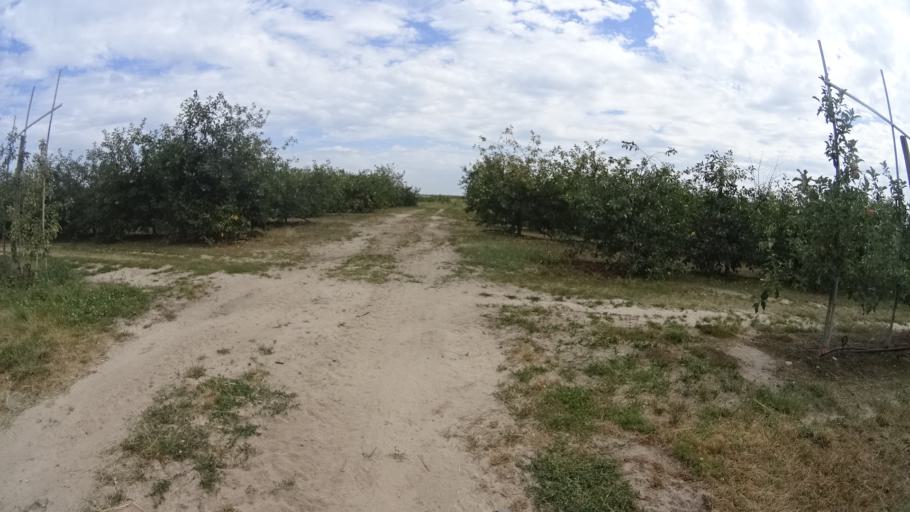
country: PL
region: Masovian Voivodeship
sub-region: Powiat bialobrzeski
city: Wysmierzyce
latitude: 51.6554
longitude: 20.7992
